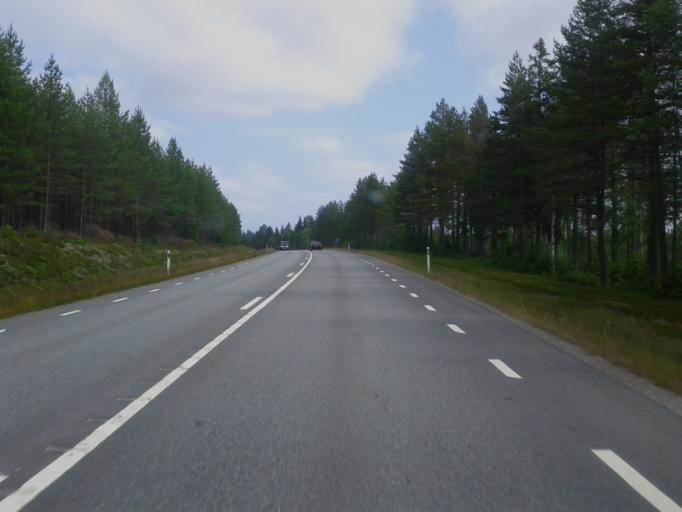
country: SE
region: Vaesterbotten
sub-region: Skelleftea Kommun
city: Burea
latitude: 64.3477
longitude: 21.2900
